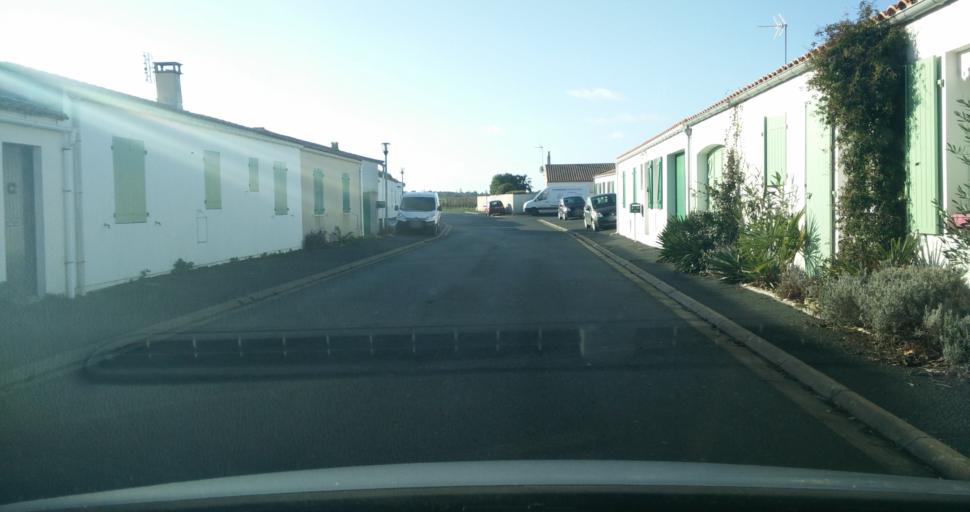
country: FR
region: Poitou-Charentes
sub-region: Departement de la Charente-Maritime
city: Saint-Martin-de-Re
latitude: 46.1979
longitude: -1.3593
